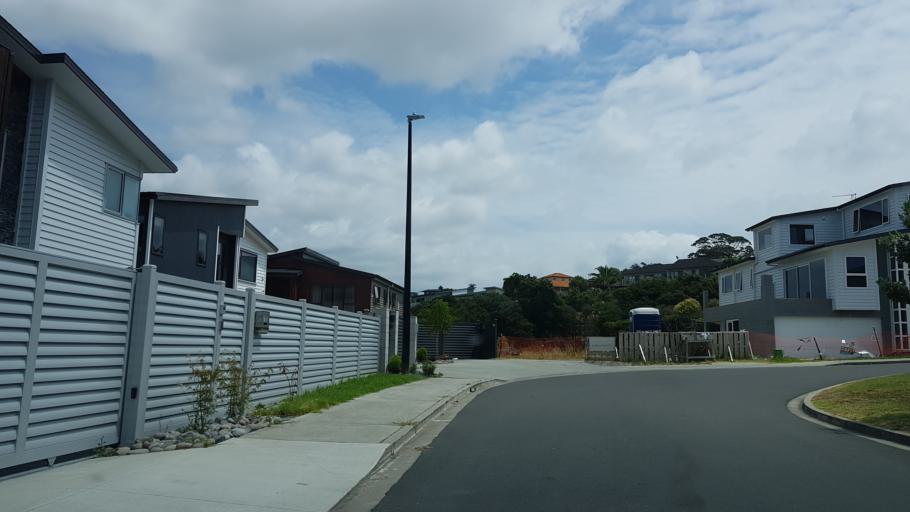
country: NZ
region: Auckland
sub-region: Auckland
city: Rosebank
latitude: -36.8009
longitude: 174.6515
